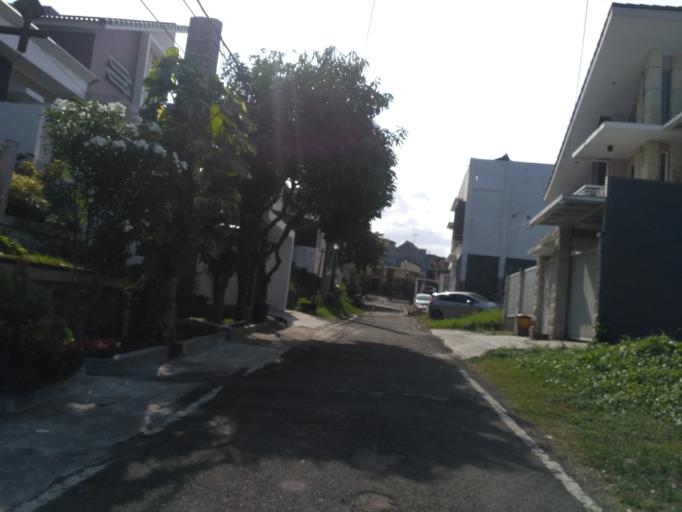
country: ID
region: East Java
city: Malang
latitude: -7.9352
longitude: 112.6085
